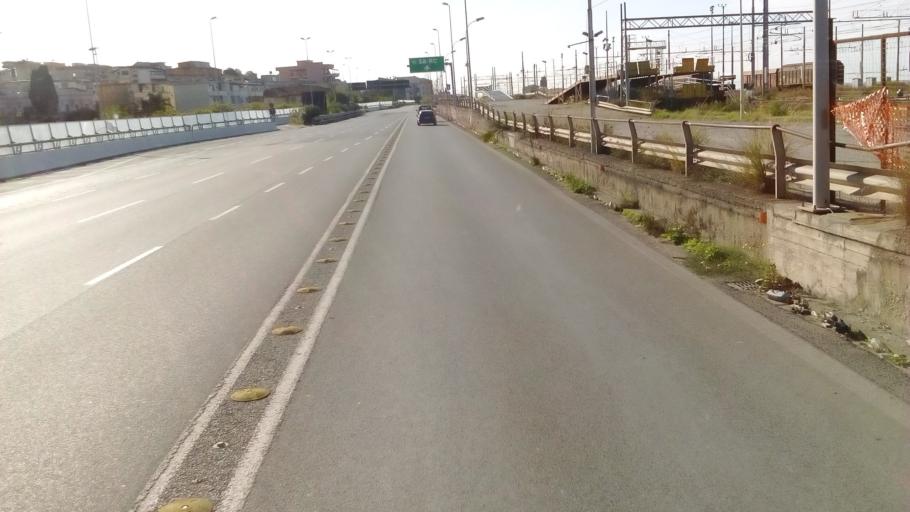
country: IT
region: Calabria
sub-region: Provincia di Reggio Calabria
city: Campo Calabro
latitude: 38.2135
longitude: 15.6352
